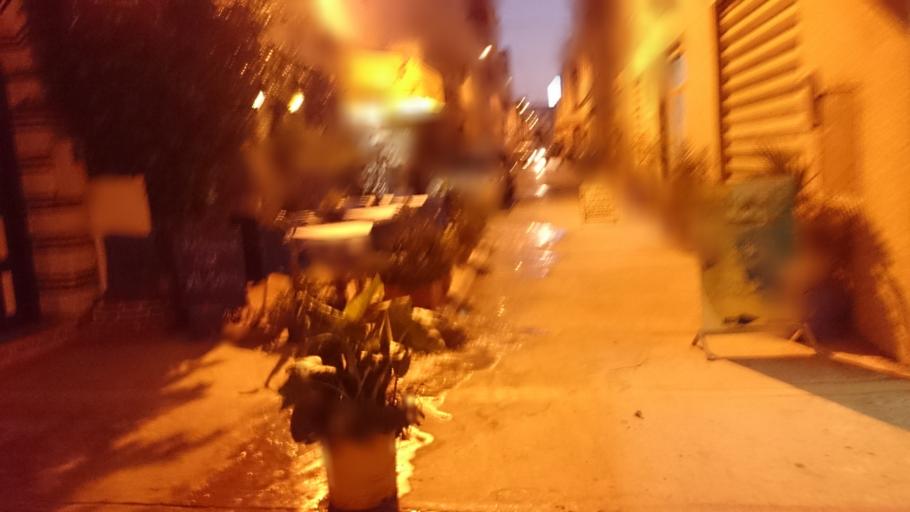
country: MA
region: Tanger-Tetouan
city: Asilah
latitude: 35.4663
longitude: -6.0340
